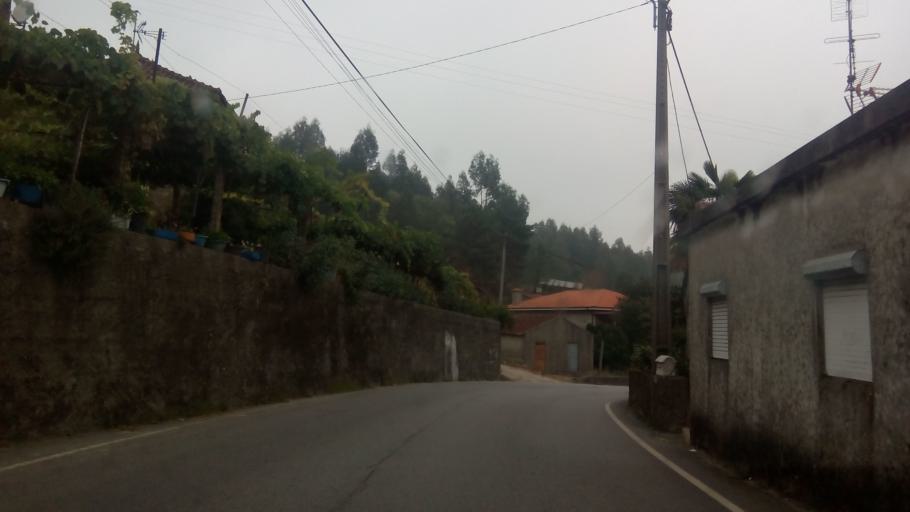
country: PT
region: Porto
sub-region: Paredes
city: Rebordosa
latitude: 41.2149
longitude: -8.3848
